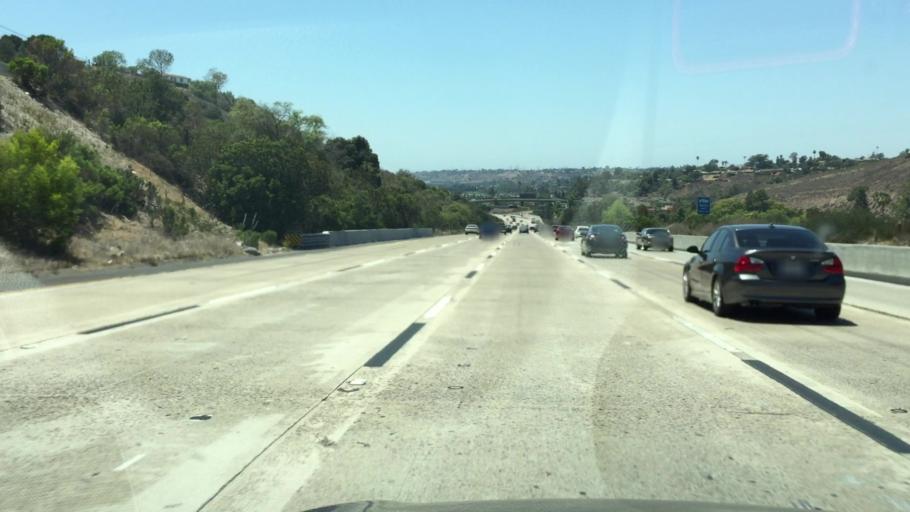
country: US
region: California
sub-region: San Diego County
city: La Mesa
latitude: 32.7798
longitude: -117.0775
